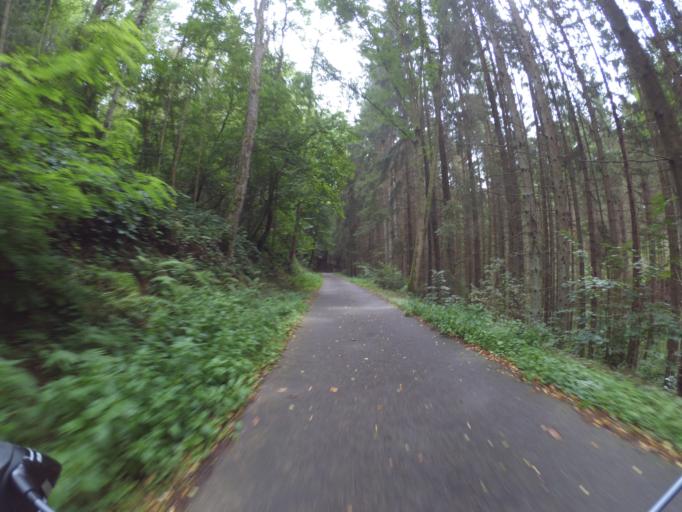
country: DE
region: Rheinland-Pfalz
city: Beilingen
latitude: 49.9610
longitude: 6.6709
